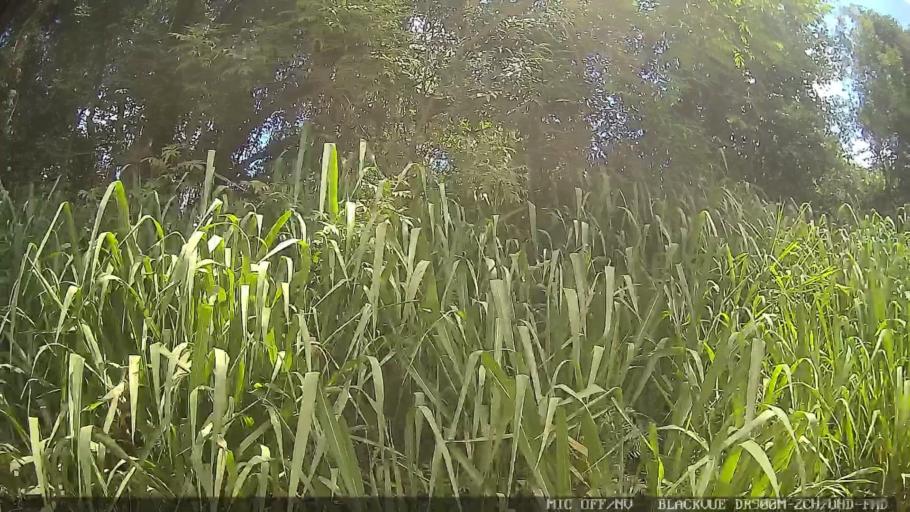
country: BR
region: Sao Paulo
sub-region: Atibaia
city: Atibaia
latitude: -23.1537
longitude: -46.6114
